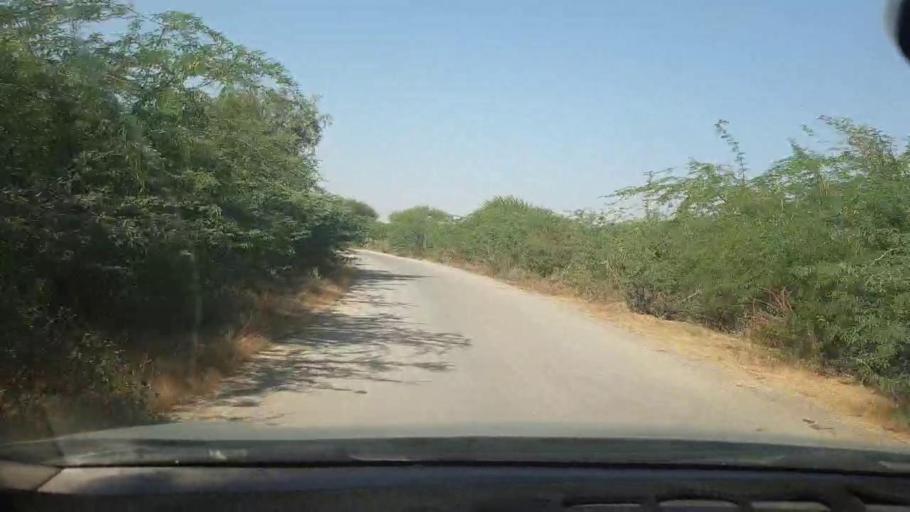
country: PK
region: Sindh
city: Malir Cantonment
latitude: 25.1618
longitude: 67.1604
